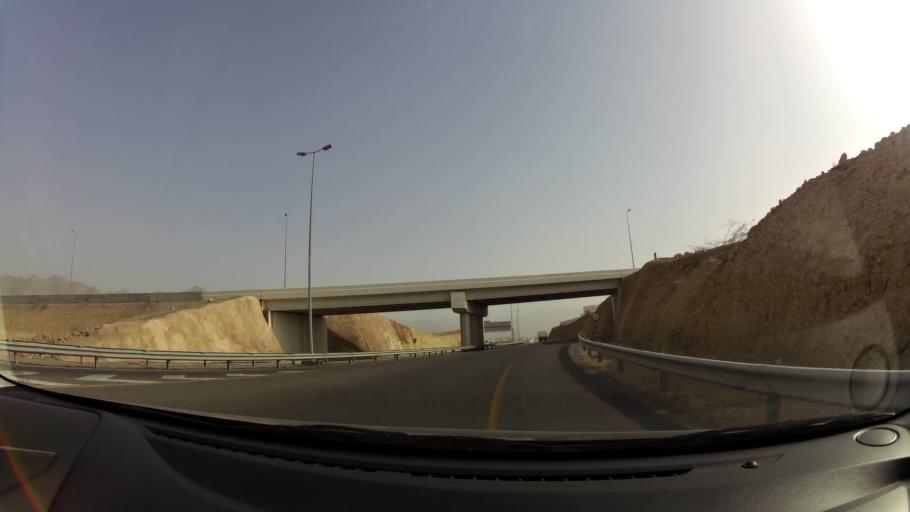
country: OM
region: Muhafazat Masqat
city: Bawshar
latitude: 23.5565
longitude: 58.3691
